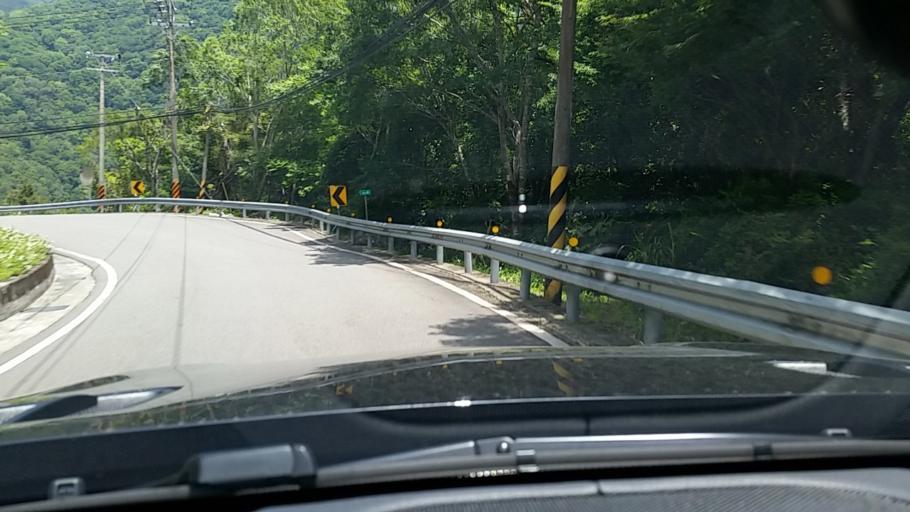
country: TW
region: Taiwan
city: Daxi
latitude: 24.6969
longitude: 121.3761
